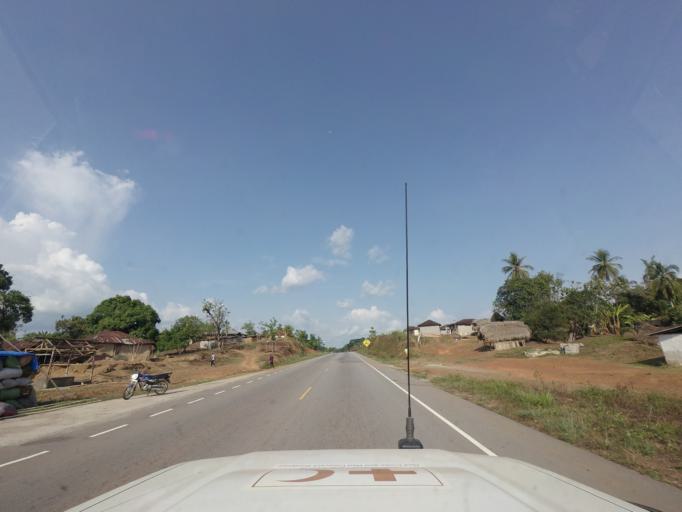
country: LR
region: Bong
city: Gbarnga
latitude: 6.8395
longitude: -9.8449
